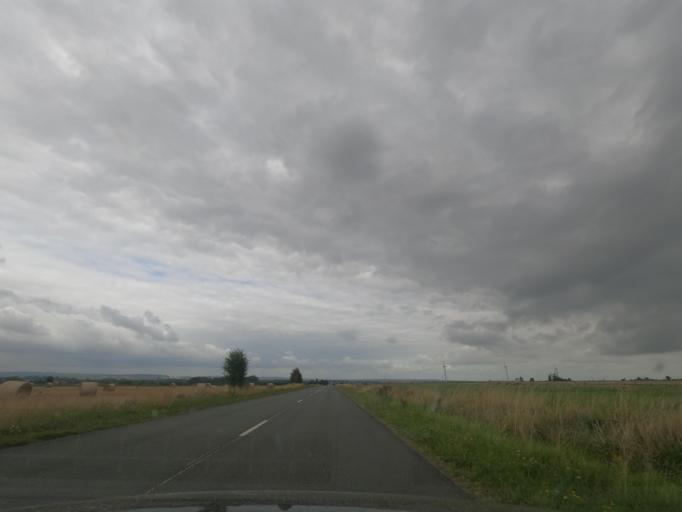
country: FR
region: Lower Normandy
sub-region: Departement de l'Orne
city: Ecouche
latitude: 48.7178
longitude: -0.0869
